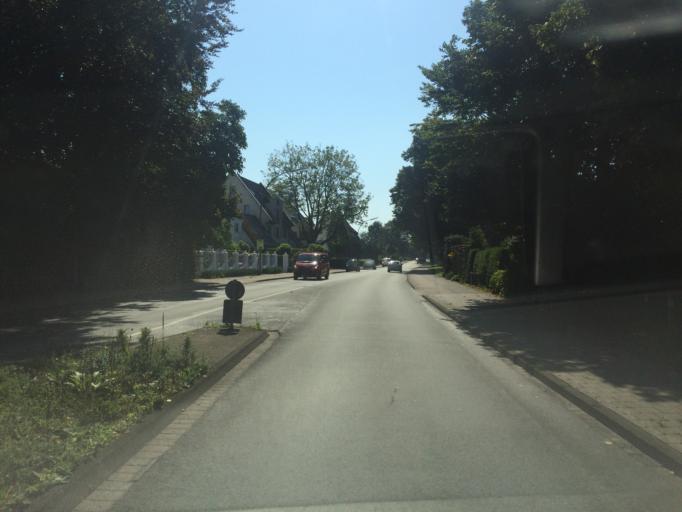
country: DE
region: North Rhine-Westphalia
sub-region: Regierungsbezirk Munster
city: Muenster
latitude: 51.9843
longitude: 7.7017
